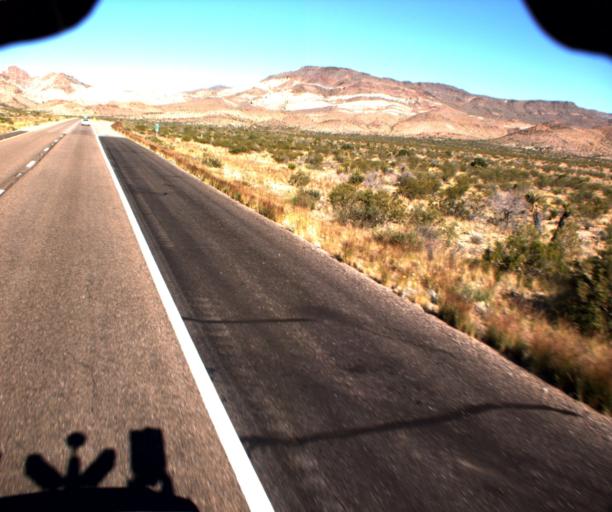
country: US
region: Arizona
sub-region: Mohave County
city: Golden Valley
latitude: 35.2289
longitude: -114.3563
